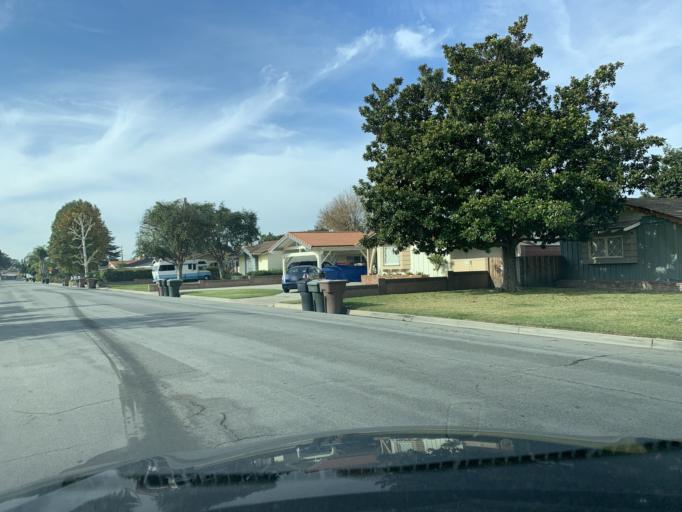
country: US
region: California
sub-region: Orange County
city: Garden Grove
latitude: 33.7847
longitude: -117.9335
